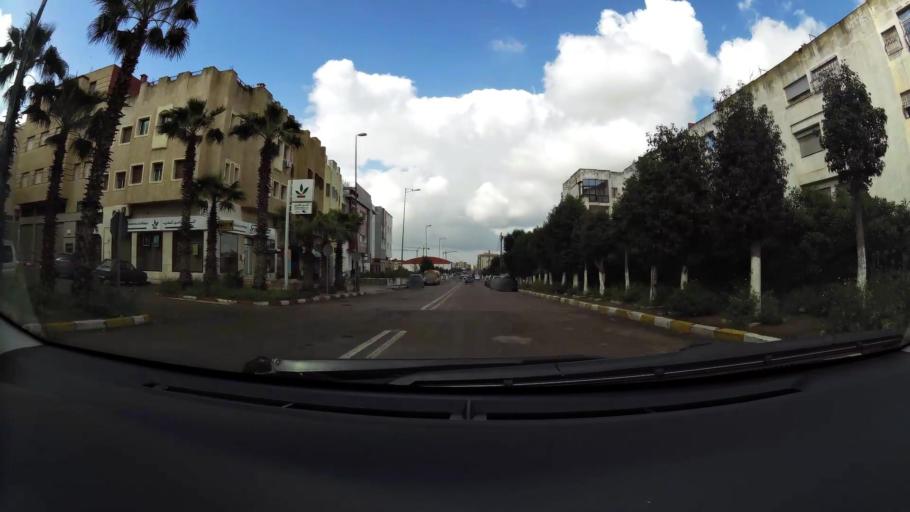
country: MA
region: Grand Casablanca
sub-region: Mediouna
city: Tit Mellil
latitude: 33.5526
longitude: -7.4774
